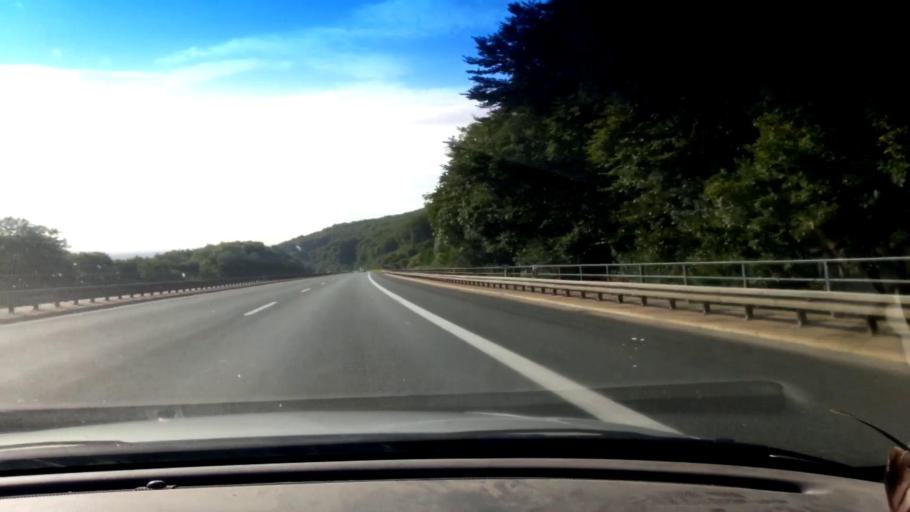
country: DE
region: Bavaria
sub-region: Upper Franconia
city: Schesslitz
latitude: 49.9835
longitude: 11.0873
